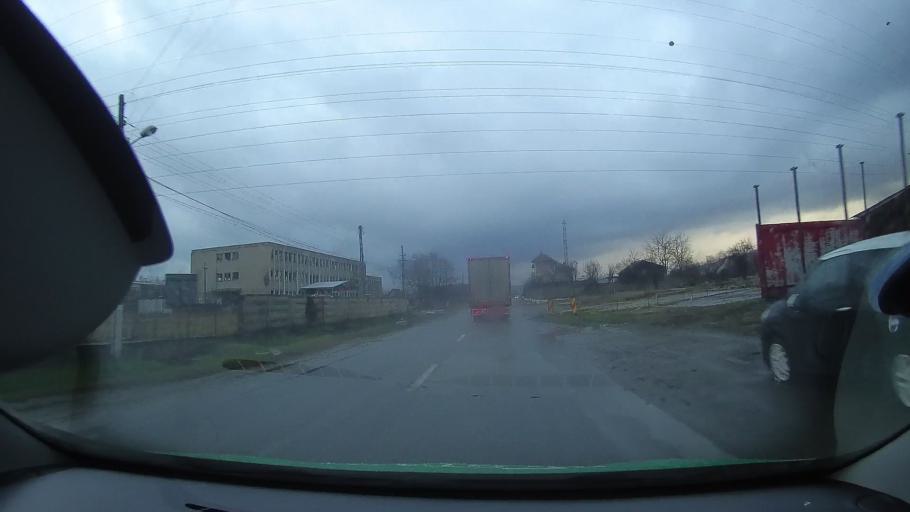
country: RO
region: Hunedoara
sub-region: Municipiul Brad
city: Brad
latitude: 46.1442
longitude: 22.7745
